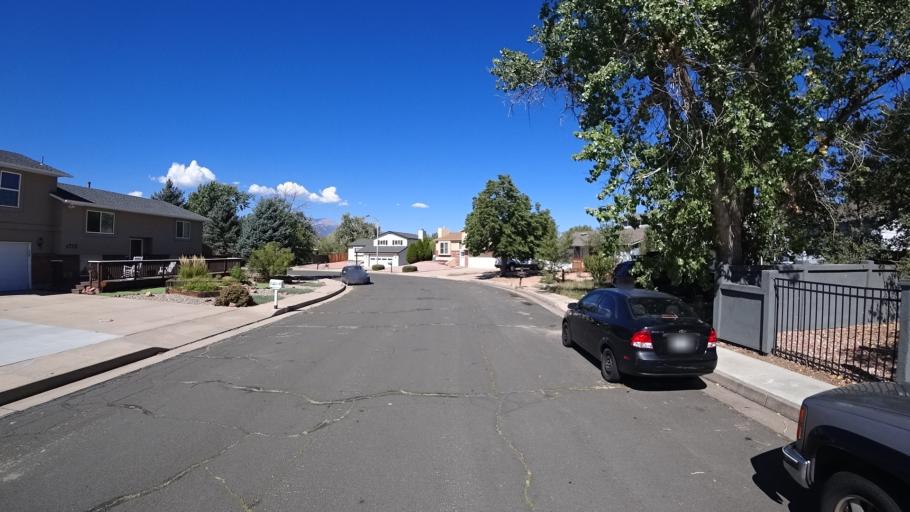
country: US
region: Colorado
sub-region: El Paso County
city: Stratmoor
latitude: 38.8154
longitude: -104.7409
